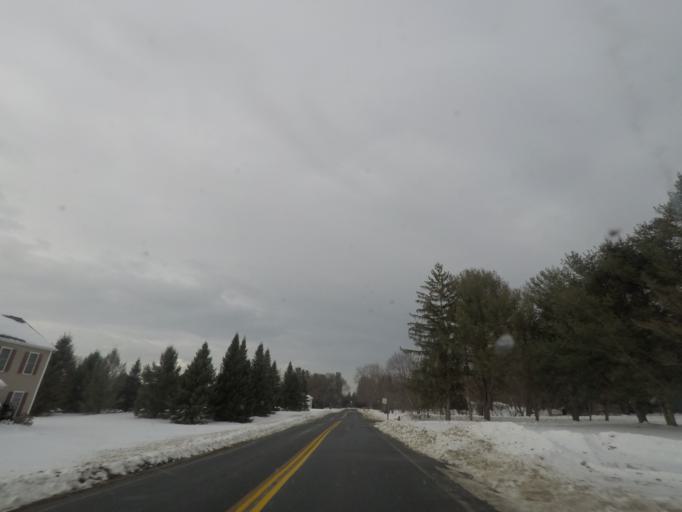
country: US
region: New York
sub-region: Rensselaer County
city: Castleton-on-Hudson
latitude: 42.5161
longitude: -73.6920
